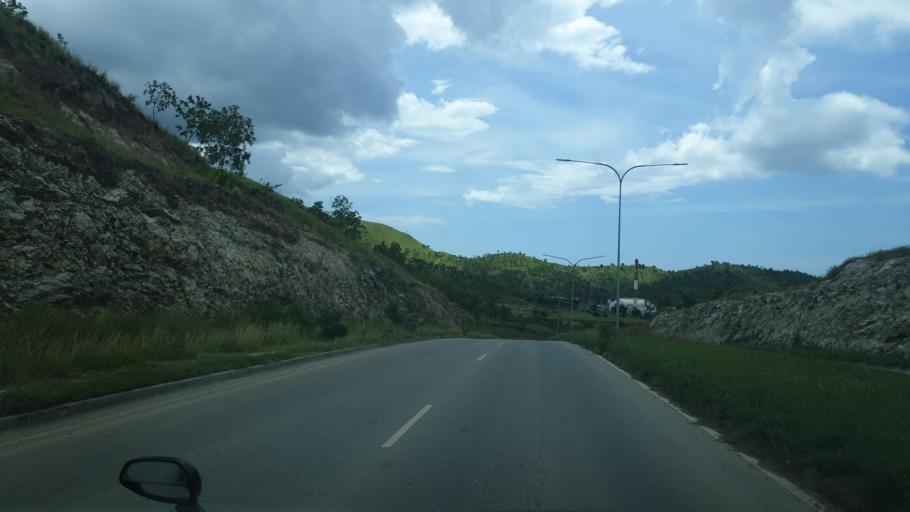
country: PG
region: National Capital
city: Port Moresby
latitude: -9.4244
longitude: 147.1402
